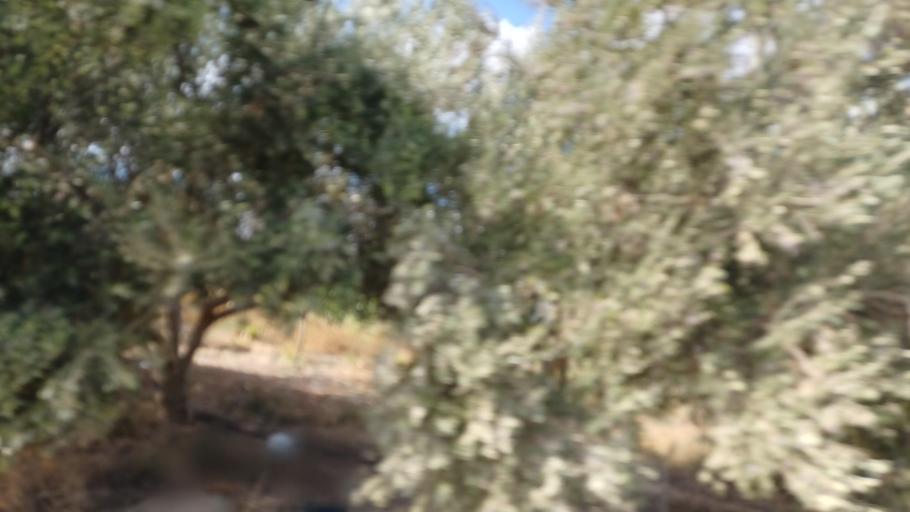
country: CY
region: Limassol
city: Pissouri
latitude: 34.6999
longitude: 32.5557
